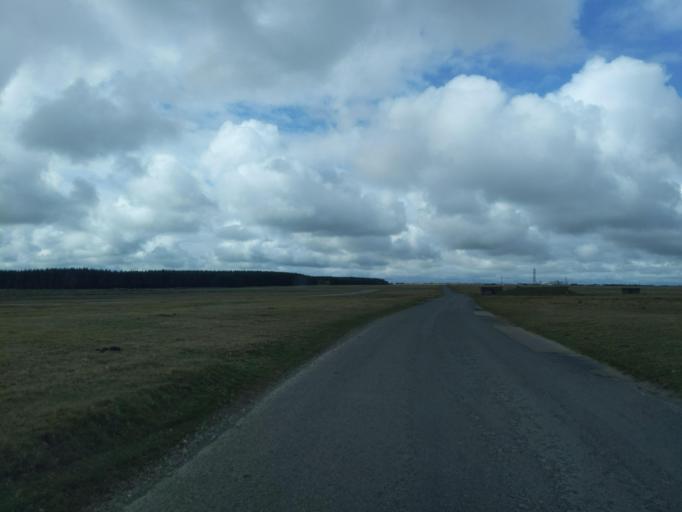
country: GB
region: England
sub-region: Cornwall
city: Camelford
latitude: 50.6310
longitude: -4.6067
